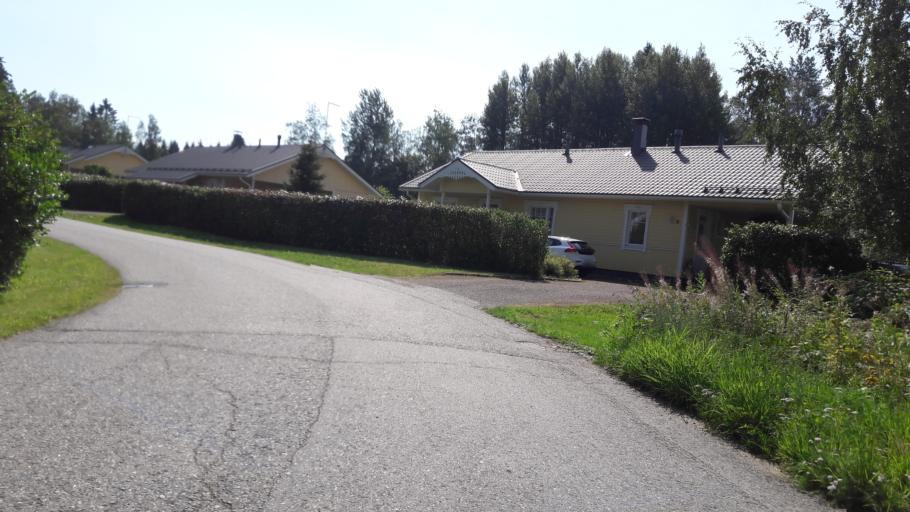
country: FI
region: North Karelia
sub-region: Joensuu
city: Joensuu
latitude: 62.5268
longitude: 29.8367
